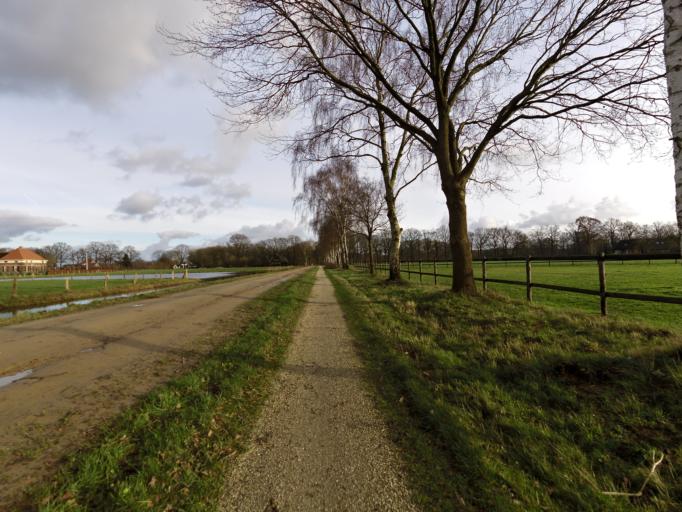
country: NL
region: Gelderland
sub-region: Gemeente Bronckhorst
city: Zelhem
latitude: 51.9730
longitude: 6.3403
